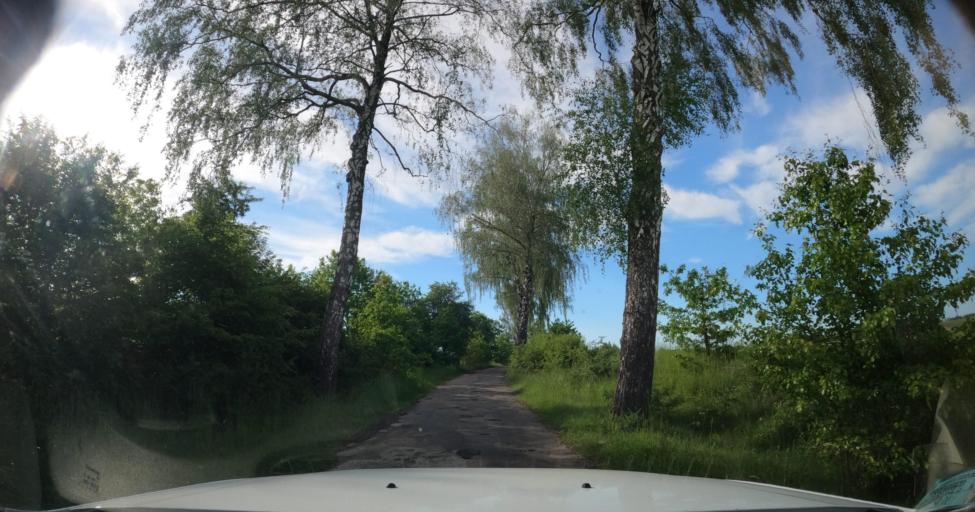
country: PL
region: Warmian-Masurian Voivodeship
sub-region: Powiat ostrodzki
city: Morag
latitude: 54.0528
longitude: 19.8899
